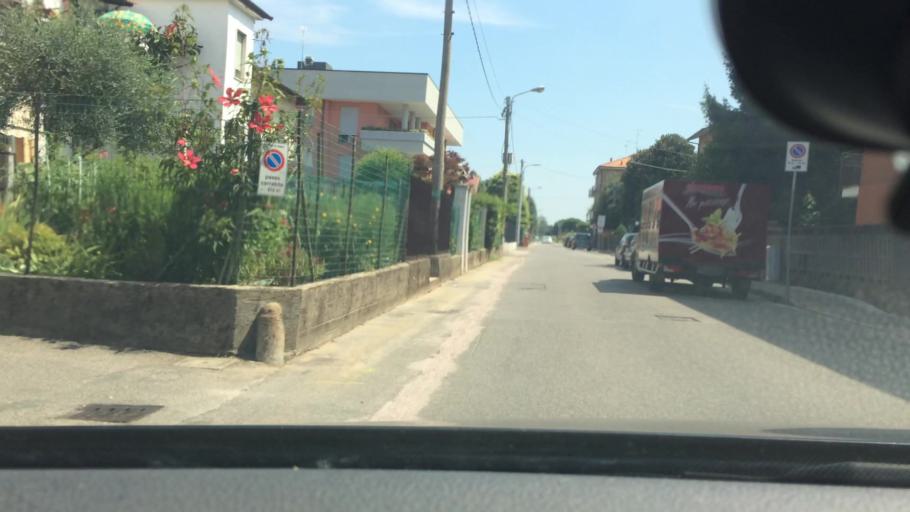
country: IT
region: Lombardy
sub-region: Provincia di Como
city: Turate
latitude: 45.6559
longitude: 9.0074
